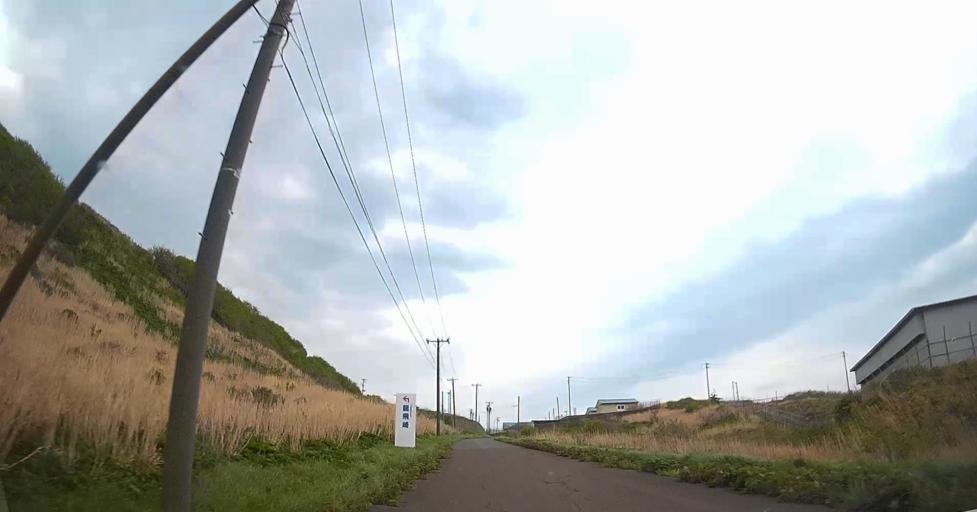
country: JP
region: Aomori
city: Shimokizukuri
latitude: 41.2554
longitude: 140.3432
